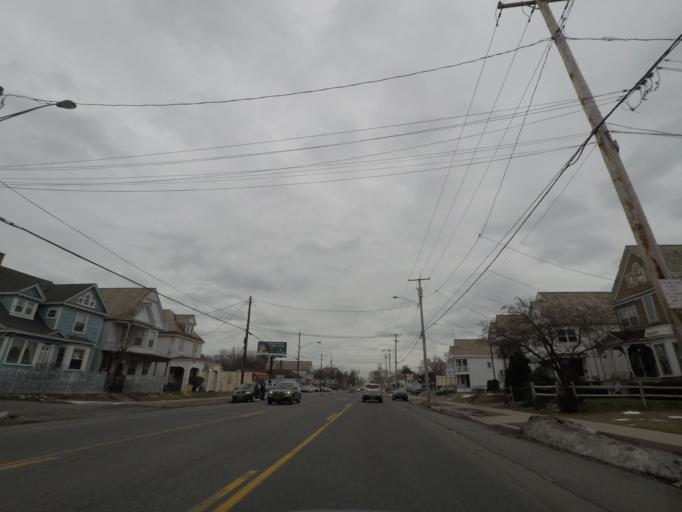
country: US
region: New York
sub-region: Schenectady County
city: Schenectady
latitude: 42.7933
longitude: -73.9186
